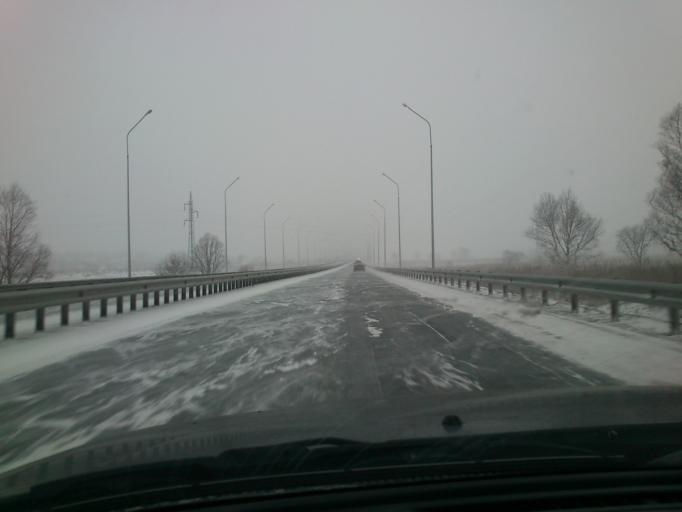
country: RU
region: Primorskiy
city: Uglovoye
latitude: 43.3553
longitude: 132.1257
